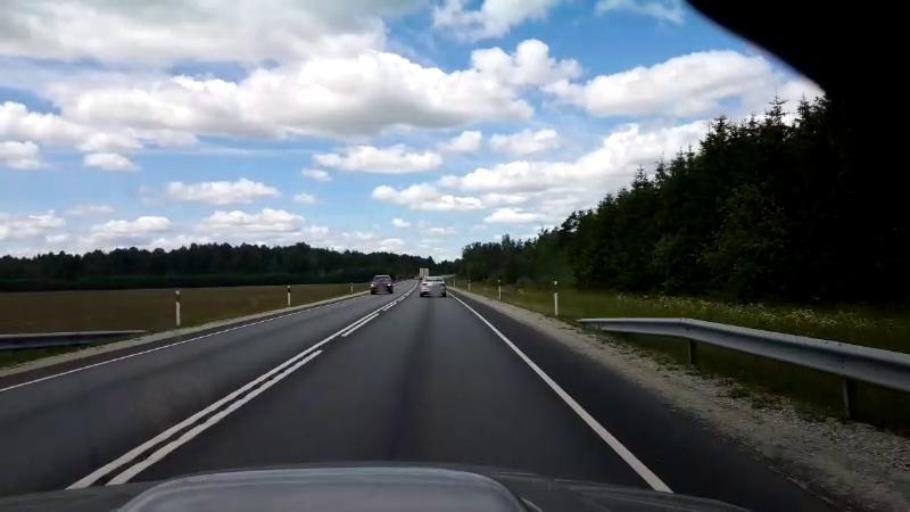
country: EE
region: Paernumaa
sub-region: Halinga vald
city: Parnu-Jaagupi
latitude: 58.6710
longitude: 24.4492
